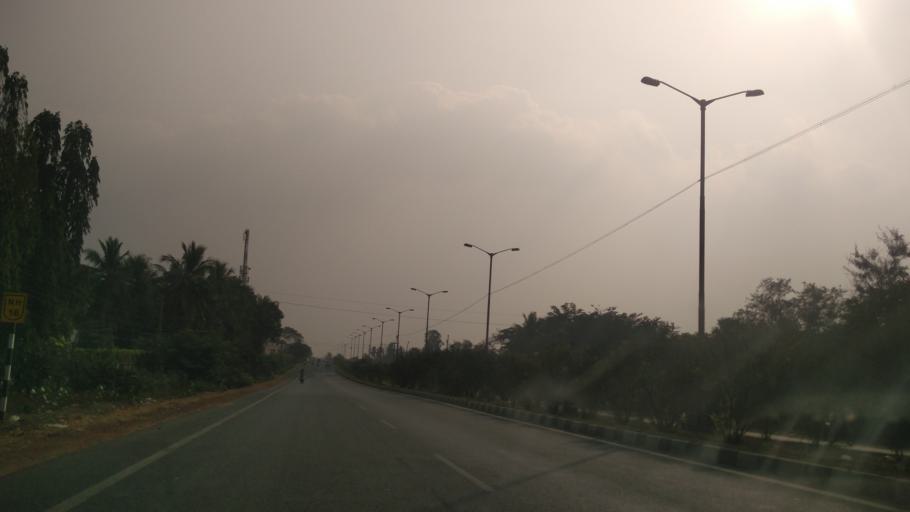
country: IN
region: Andhra Pradesh
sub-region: East Godavari
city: Rajahmundry
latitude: 16.9603
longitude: 81.7945
